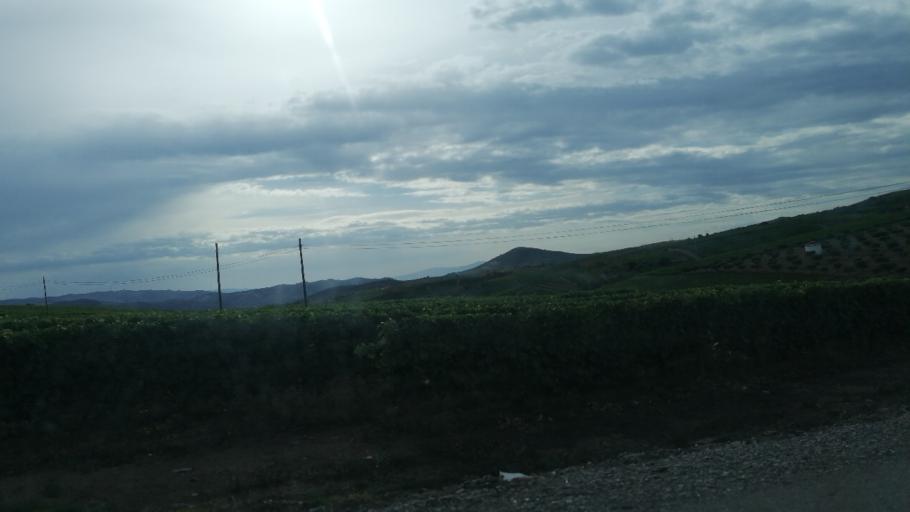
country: PT
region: Viseu
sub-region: Sao Joao da Pesqueira
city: Sao Joao da Pesqueira
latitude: 41.1305
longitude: -7.3982
